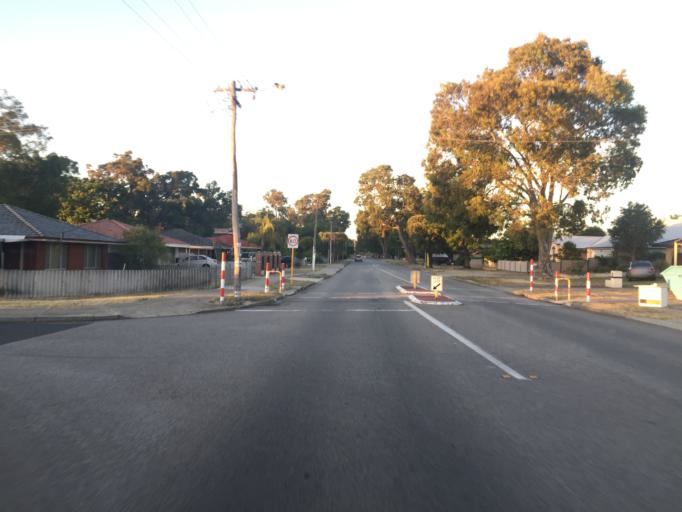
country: AU
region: Western Australia
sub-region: Gosnells
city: Kenwick
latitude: -32.0326
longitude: 115.9821
